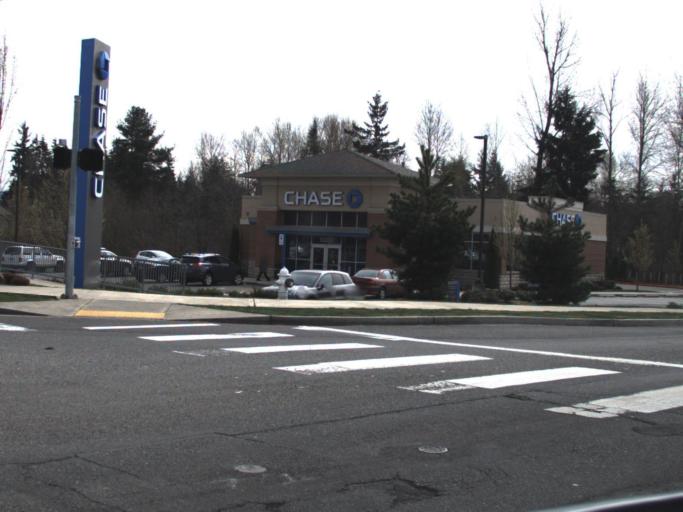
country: US
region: Washington
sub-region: King County
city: Lea Hill
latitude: 47.3580
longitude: -122.1654
